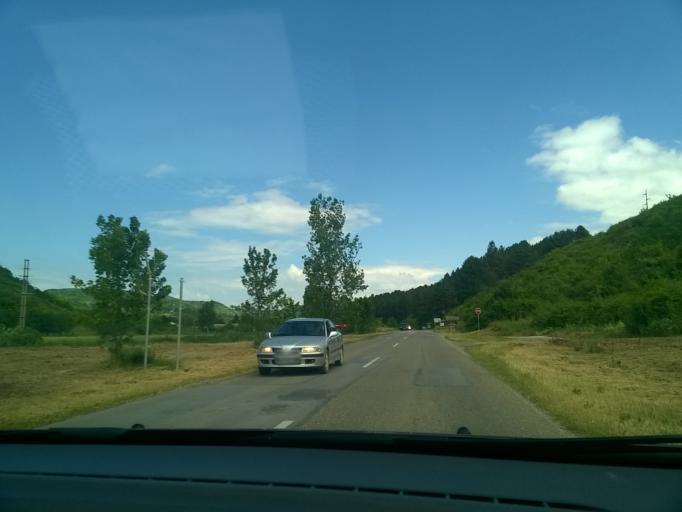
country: RS
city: Vrdnik
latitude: 45.1116
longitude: 19.8001
